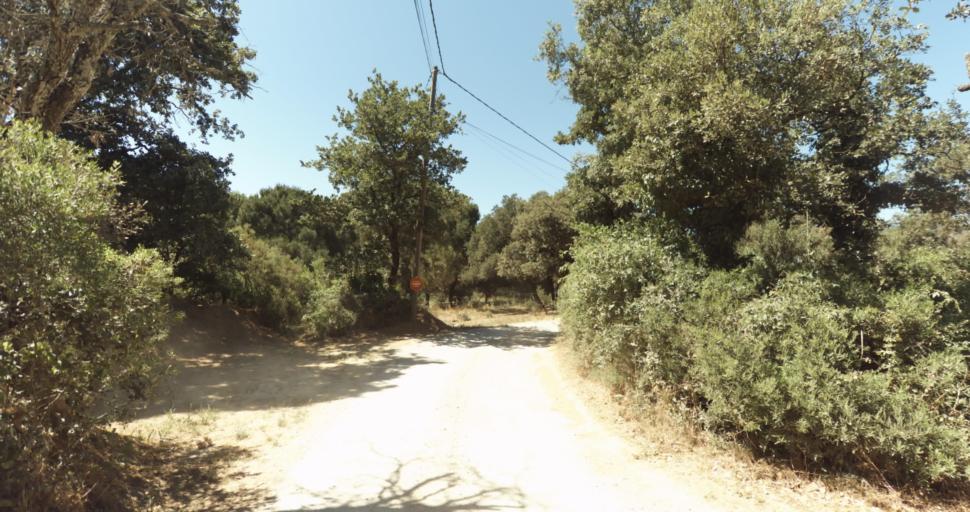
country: FR
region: Provence-Alpes-Cote d'Azur
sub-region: Departement du Var
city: Gassin
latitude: 43.2304
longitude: 6.5686
